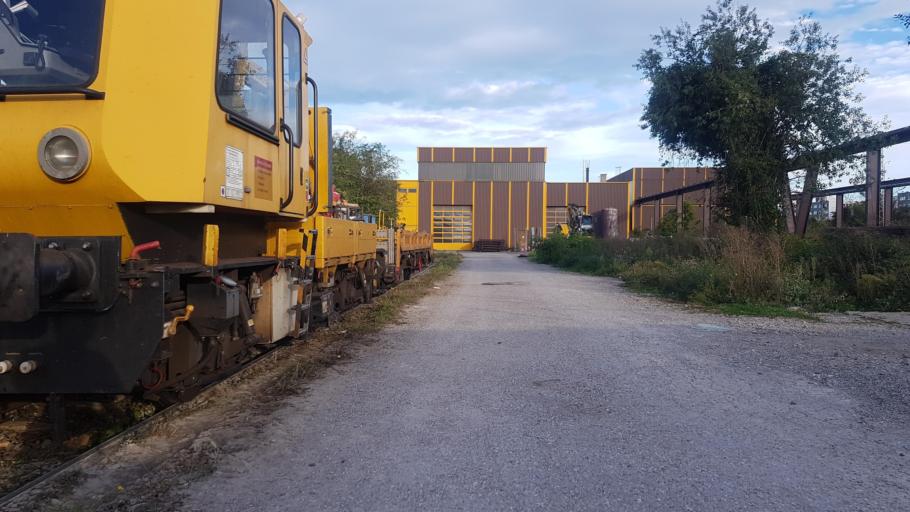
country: DE
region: Bavaria
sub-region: Upper Bavaria
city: Pasing
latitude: 48.1476
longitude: 11.4787
